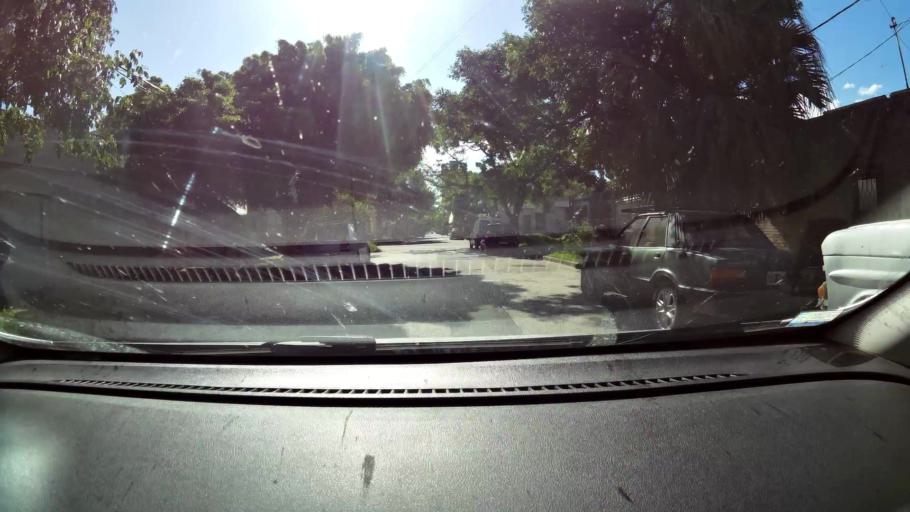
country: AR
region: Santa Fe
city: Santa Fe de la Vera Cruz
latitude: -31.6247
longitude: -60.6902
